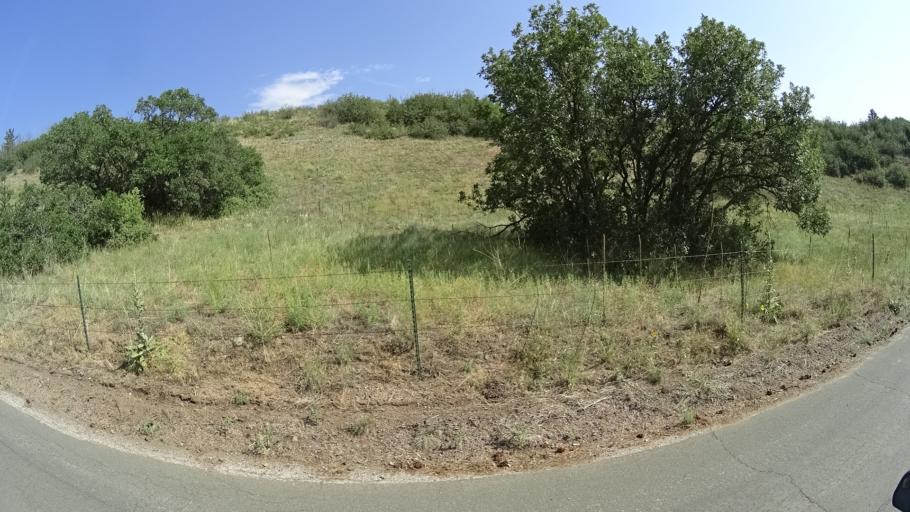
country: US
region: Colorado
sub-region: El Paso County
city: Fort Carson
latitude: 38.7206
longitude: -104.8264
